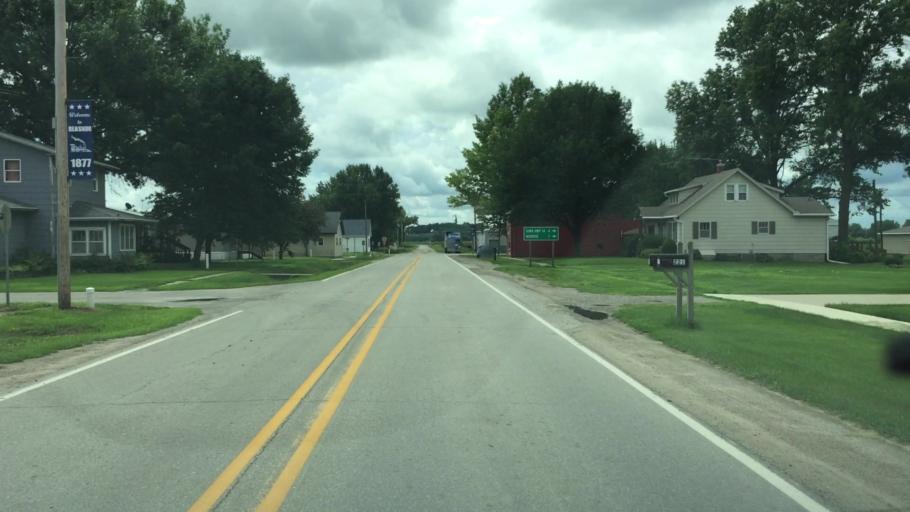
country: US
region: Iowa
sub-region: Jasper County
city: Monroe
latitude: 41.5782
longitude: -93.0235
